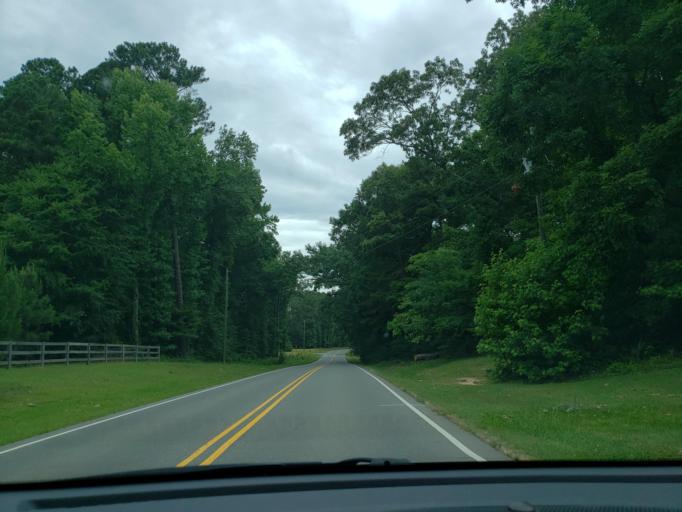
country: US
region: North Carolina
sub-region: Chatham County
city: Fearrington Village
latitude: 35.7750
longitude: -79.0052
